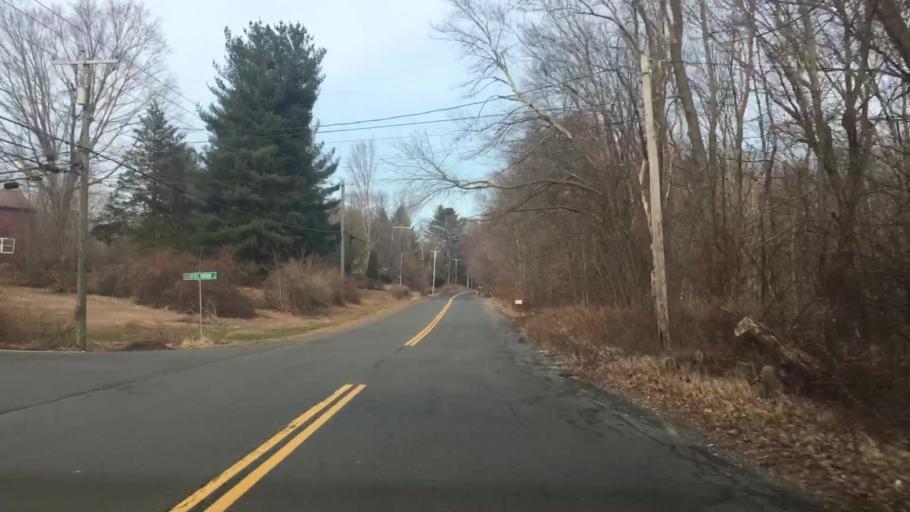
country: US
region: Connecticut
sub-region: Fairfield County
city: Newtown
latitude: 41.3697
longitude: -73.2588
